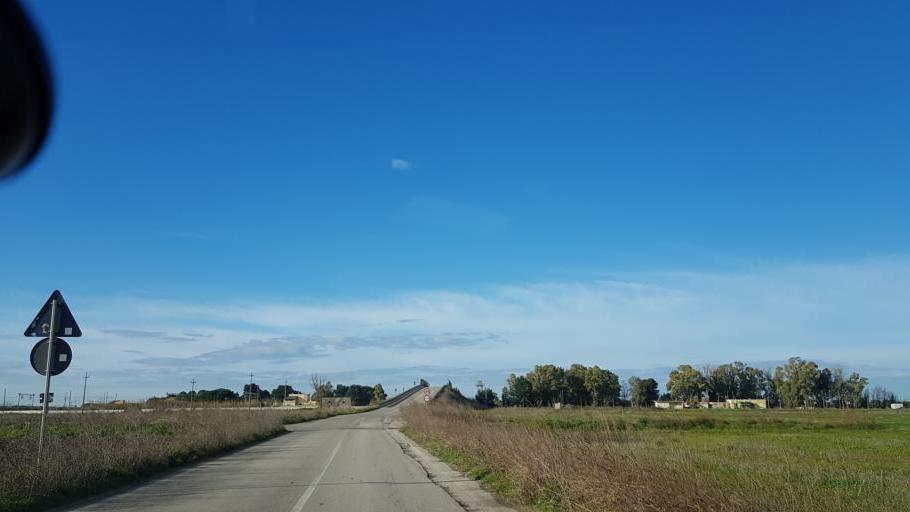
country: IT
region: Apulia
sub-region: Provincia di Brindisi
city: Tuturano
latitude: 40.5504
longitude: 17.9833
